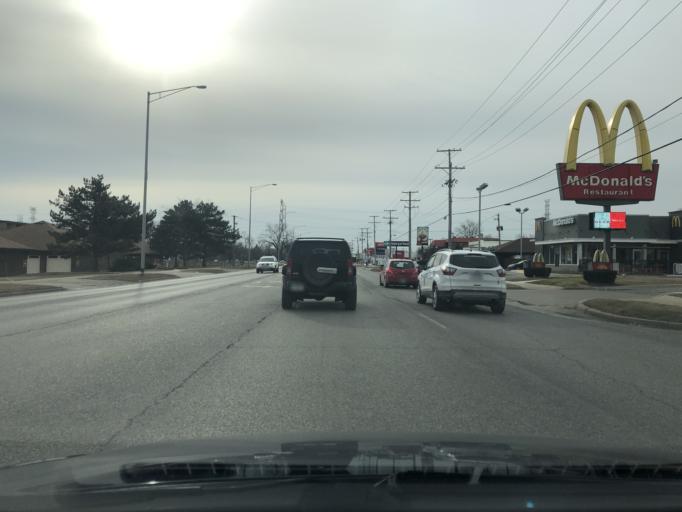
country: US
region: Illinois
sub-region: DuPage County
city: Bensenville
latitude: 41.9284
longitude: -87.9399
